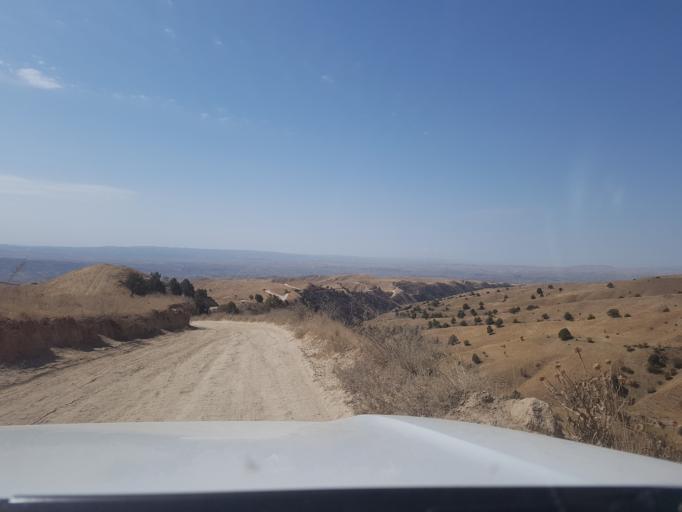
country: TM
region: Ahal
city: Baharly
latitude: 38.2840
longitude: 56.9273
